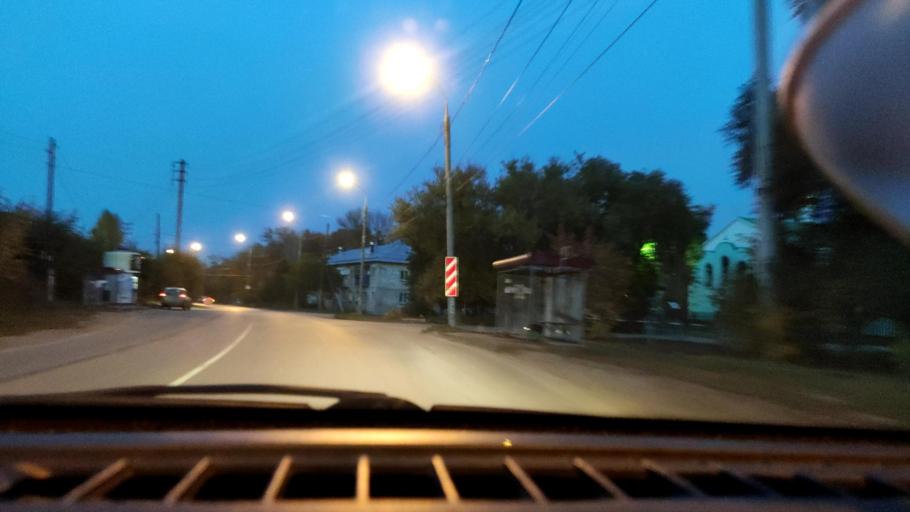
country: RU
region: Samara
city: Samara
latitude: 53.1371
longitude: 50.1245
